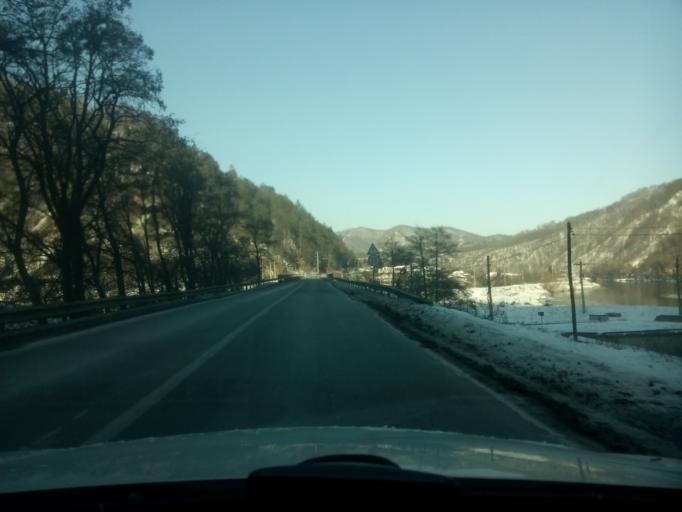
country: RO
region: Valcea
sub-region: Comuna Brezoi
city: Brezoi
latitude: 45.3351
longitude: 24.2734
